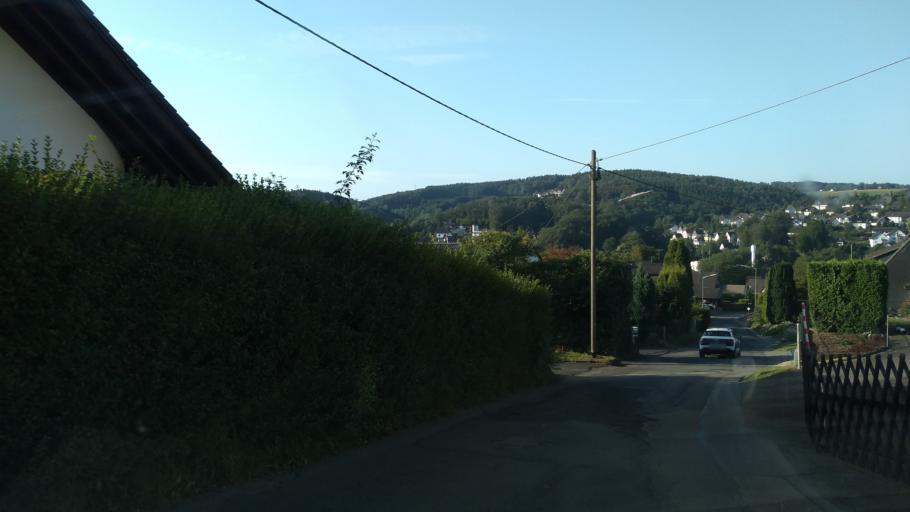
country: DE
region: North Rhine-Westphalia
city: Wiehl
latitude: 50.9663
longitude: 7.5013
